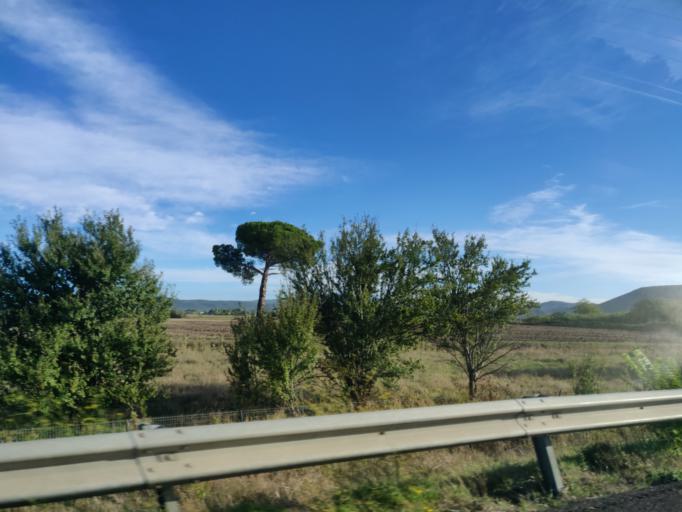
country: IT
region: Tuscany
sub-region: Provincia di Grosseto
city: Grosseto
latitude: 42.7957
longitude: 11.1092
